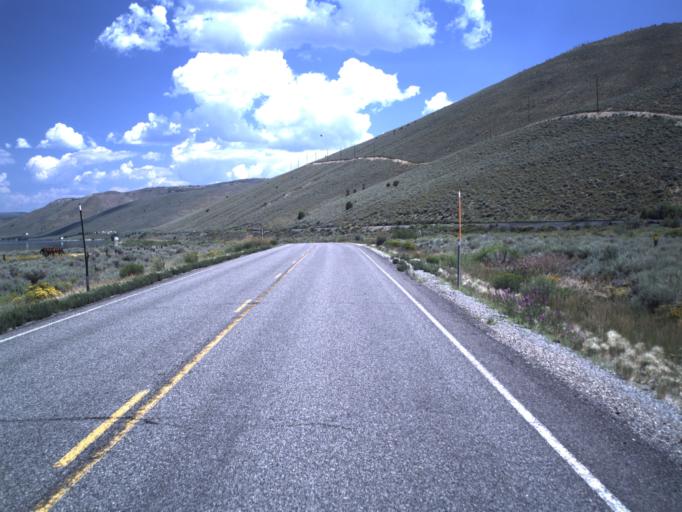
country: US
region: Utah
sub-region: Carbon County
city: Helper
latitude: 39.7614
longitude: -111.1439
